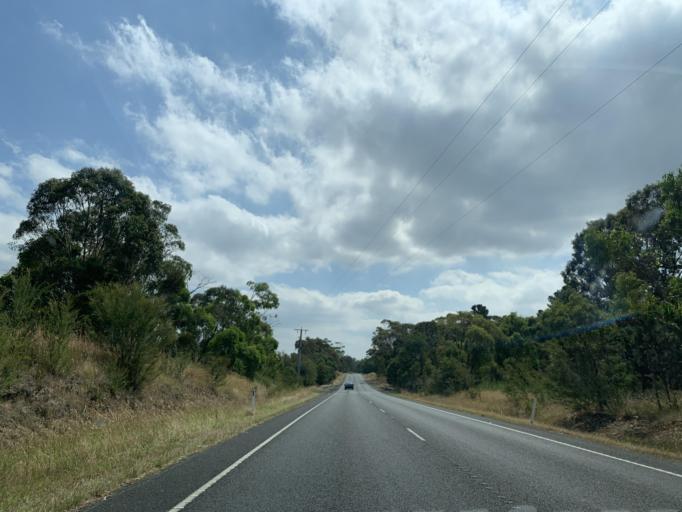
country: AU
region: Victoria
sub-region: Latrobe
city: Morwell
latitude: -38.2035
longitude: 146.4619
